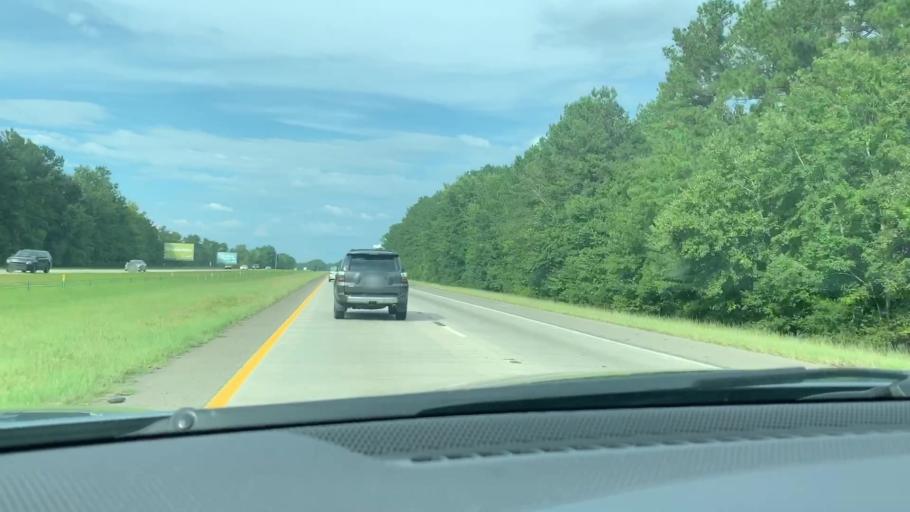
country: US
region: South Carolina
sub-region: Colleton County
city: Walterboro
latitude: 32.9512
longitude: -80.6818
